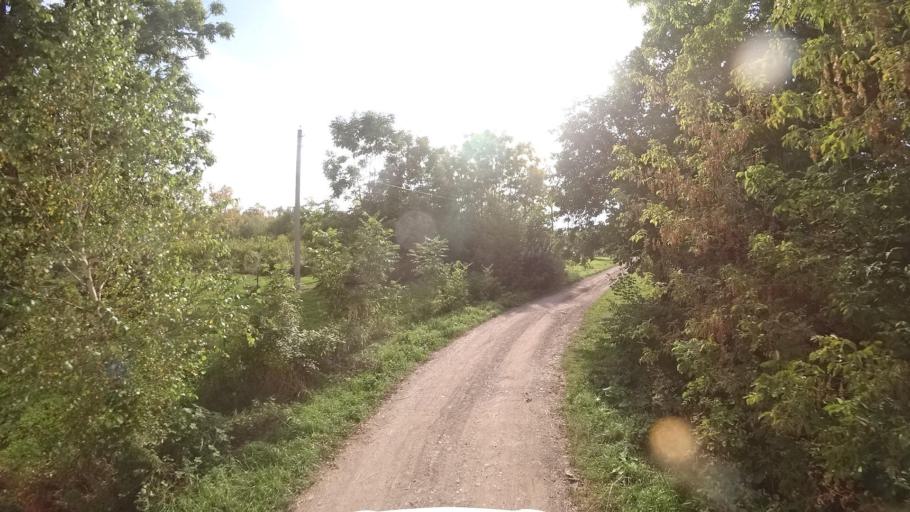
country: RU
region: Primorskiy
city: Dostoyevka
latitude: 44.2936
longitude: 133.4524
